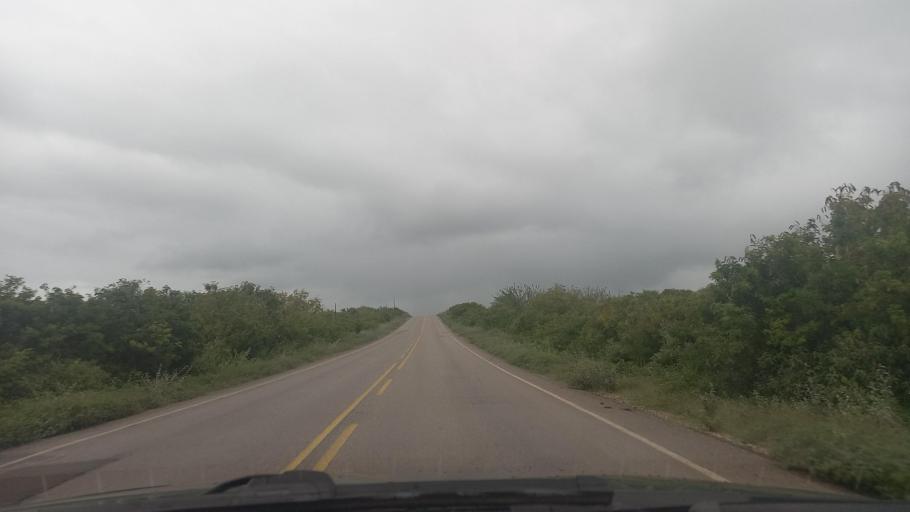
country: BR
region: Bahia
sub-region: Paulo Afonso
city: Paulo Afonso
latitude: -9.3211
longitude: -38.2901
